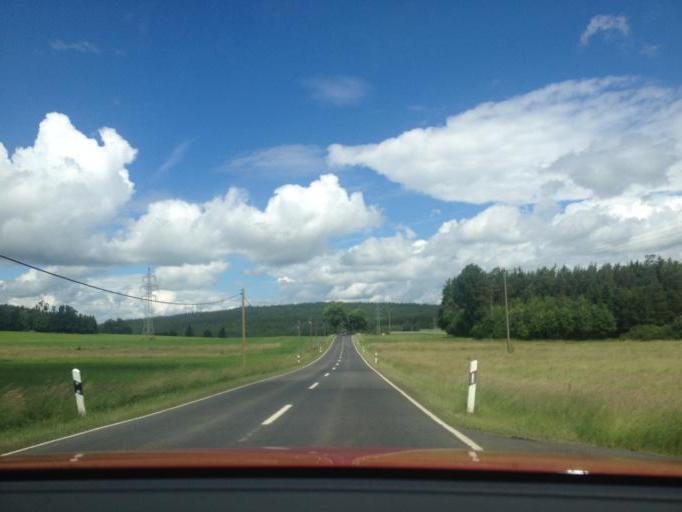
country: DE
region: Bavaria
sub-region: Upper Franconia
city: Arzberg
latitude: 50.0251
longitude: 12.2058
